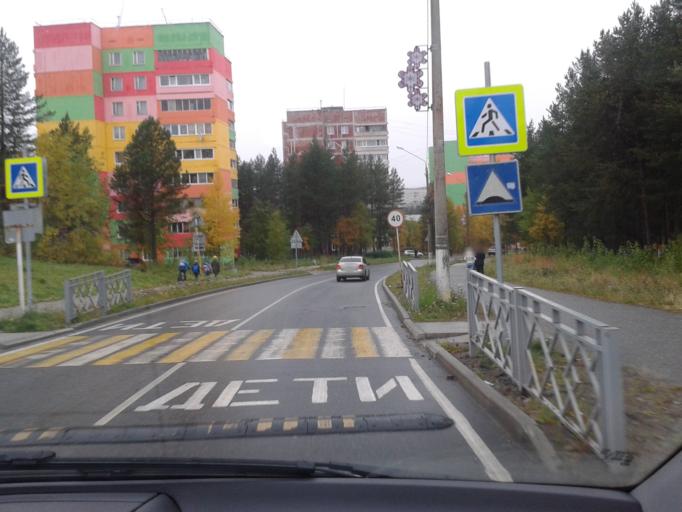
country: RU
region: Murmansk
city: Polyarnyye Zori
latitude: 67.3664
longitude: 32.4926
